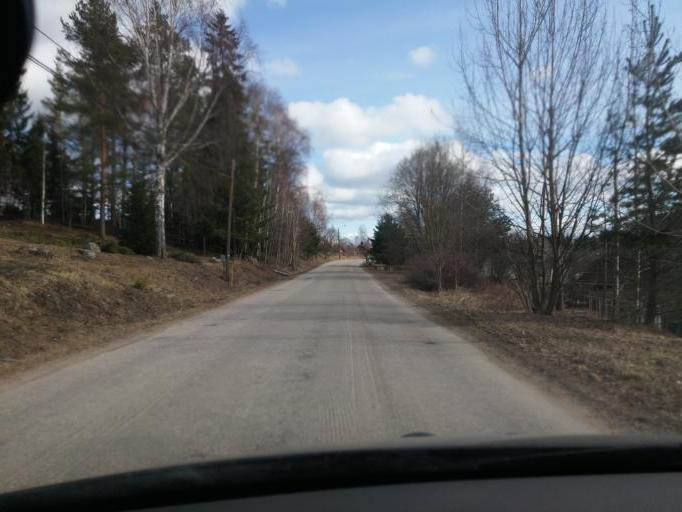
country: SE
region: Gaevleborg
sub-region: Ljusdals Kommun
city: Ljusdal
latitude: 61.8195
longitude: 16.1294
